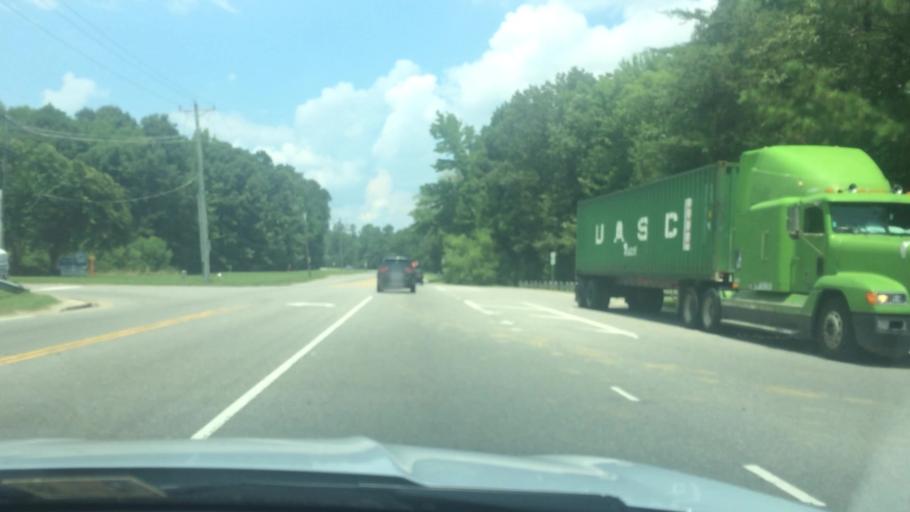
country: US
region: Virginia
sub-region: York County
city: Yorktown
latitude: 37.1772
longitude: -76.5699
